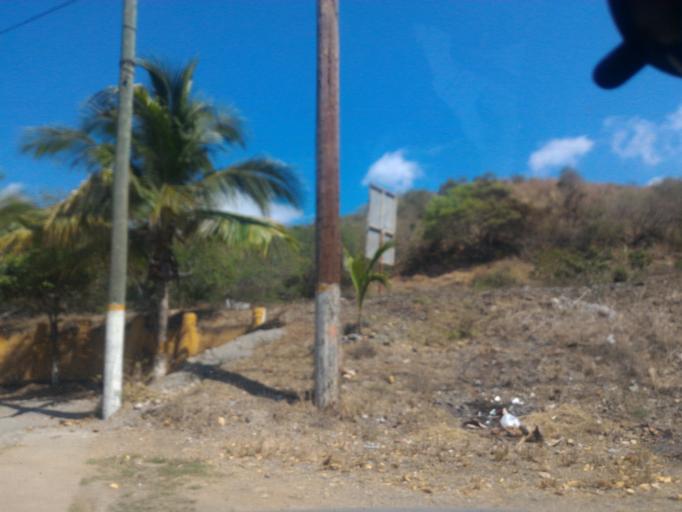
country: MX
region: Michoacan
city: Coahuayana Viejo
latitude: 18.5814
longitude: -103.6698
